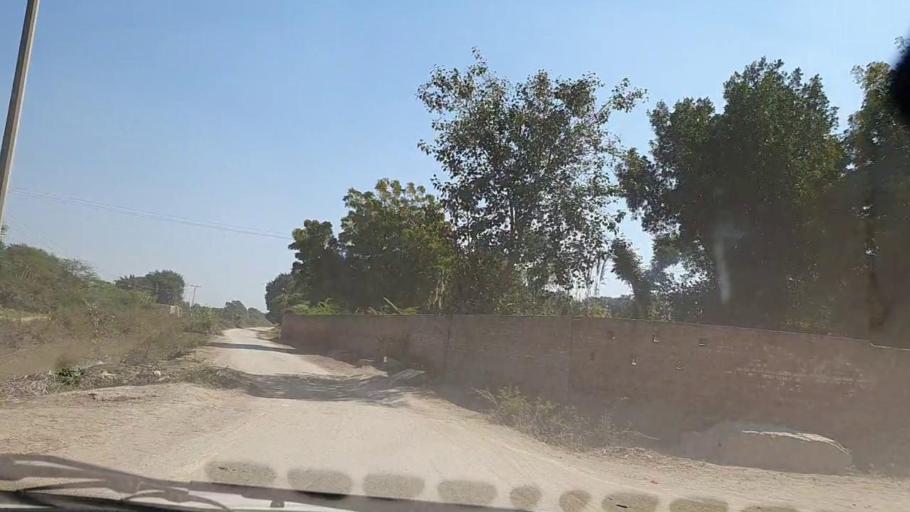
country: PK
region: Sindh
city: Mirpur Khas
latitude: 25.4713
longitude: 69.0314
